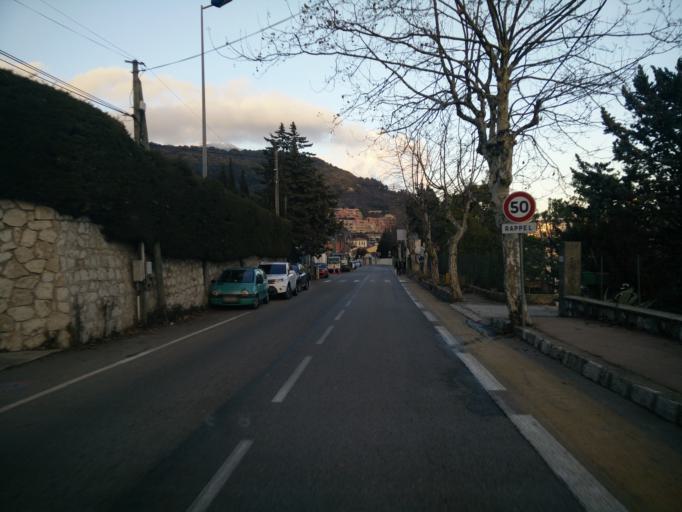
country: FR
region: Provence-Alpes-Cote d'Azur
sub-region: Departement des Alpes-Maritimes
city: La Turbie
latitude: 43.7430
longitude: 7.3920
